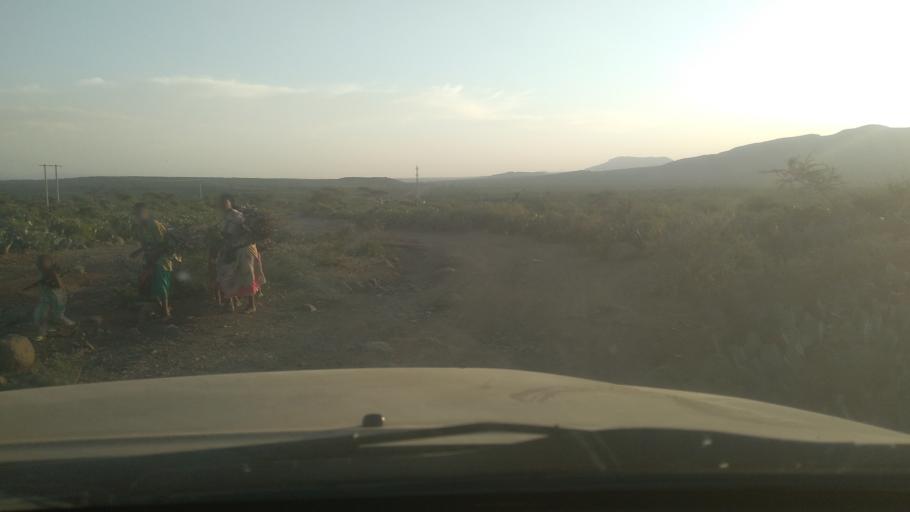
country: ET
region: Oromiya
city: Asbe Teferi
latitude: 9.2648
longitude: 40.8015
